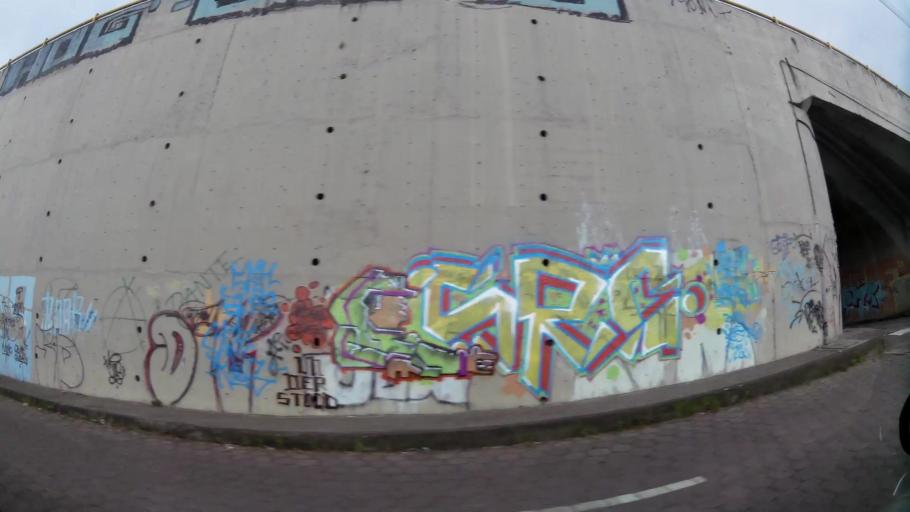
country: EC
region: Pichincha
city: Quito
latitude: -0.3038
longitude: -78.5218
